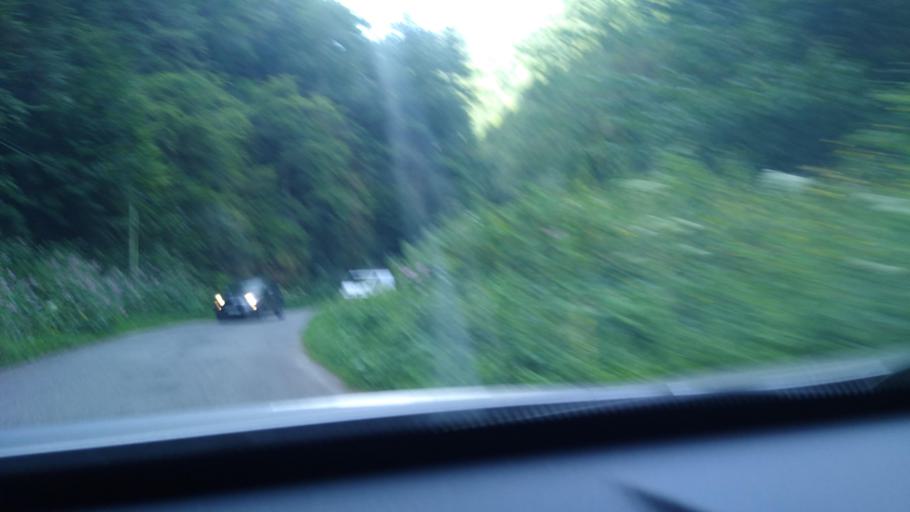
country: FR
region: Midi-Pyrenees
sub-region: Departement de l'Ariege
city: Saint-Girons
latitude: 42.8296
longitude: 1.1995
